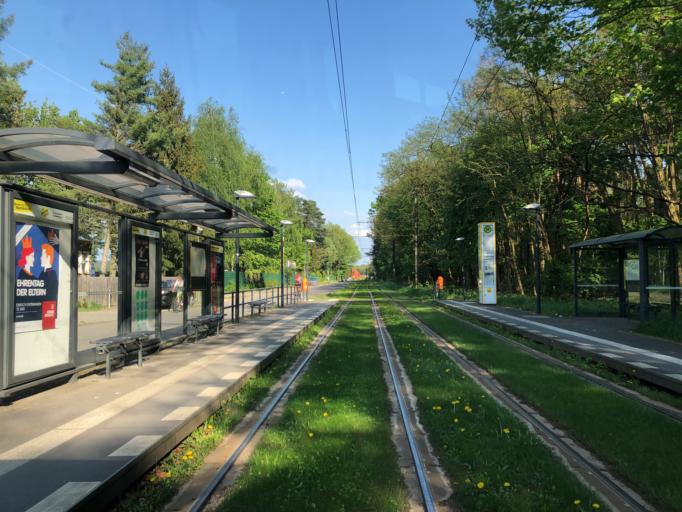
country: DE
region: Berlin
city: Grunau
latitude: 52.4087
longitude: 13.6043
